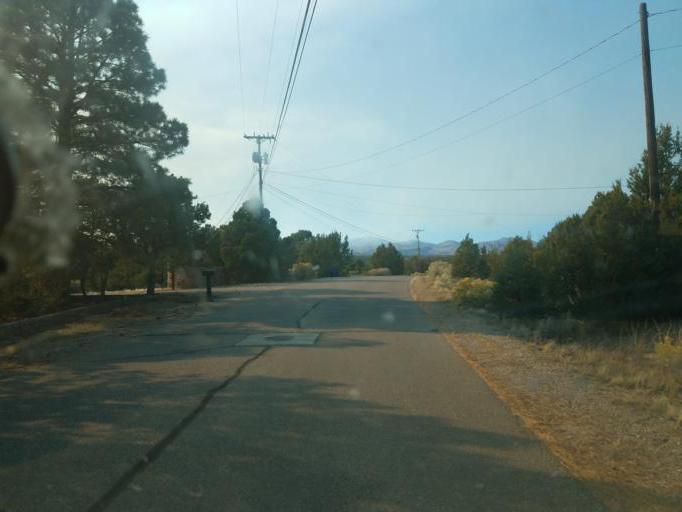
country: US
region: New Mexico
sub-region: Los Alamos County
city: White Rock
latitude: 35.8083
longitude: -106.2206
